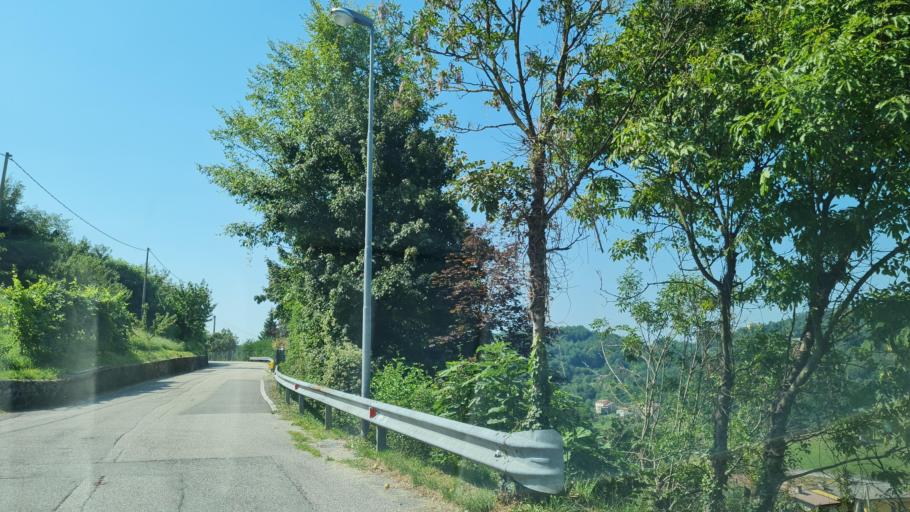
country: IT
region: Veneto
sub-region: Provincia di Vicenza
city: Salcedo
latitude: 45.7520
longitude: 11.5906
